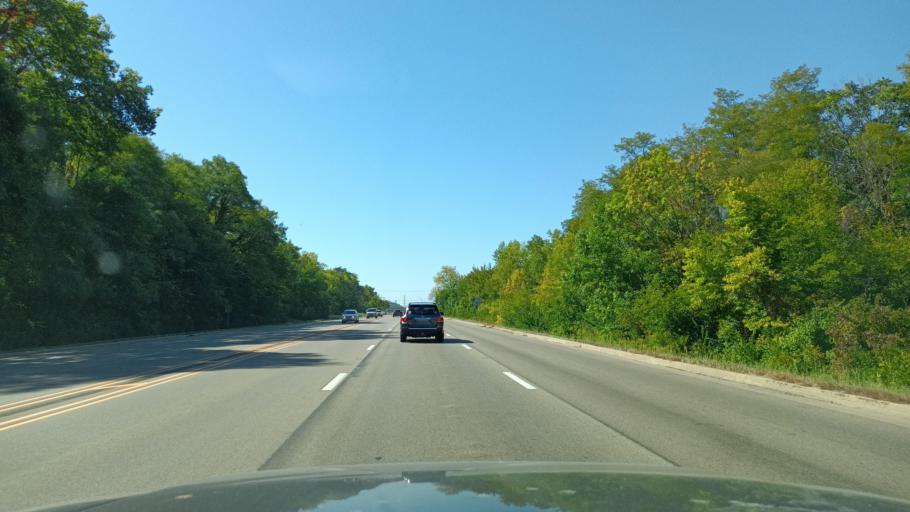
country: US
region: Illinois
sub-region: Tazewell County
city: East Peoria
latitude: 40.6753
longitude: -89.5654
